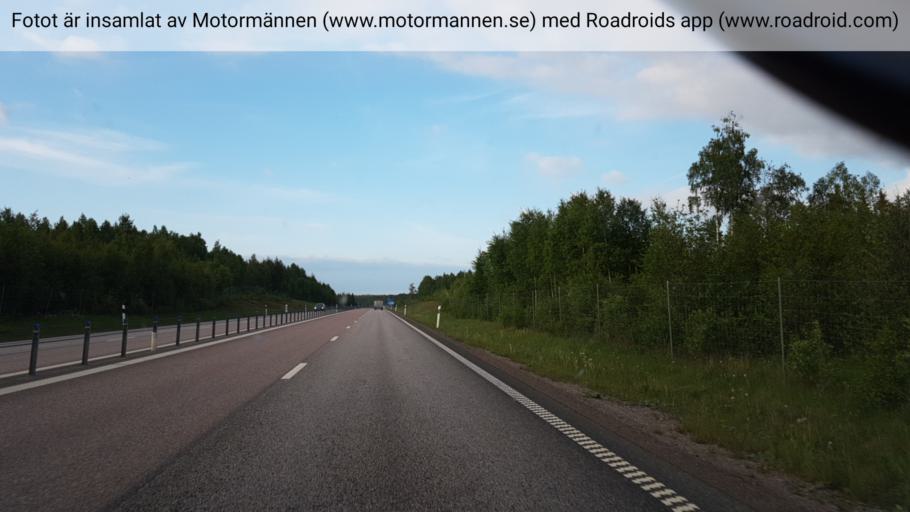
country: SE
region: Vaestra Goetaland
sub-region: Skovde Kommun
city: Skultorp
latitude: 58.3281
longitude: 13.8459
